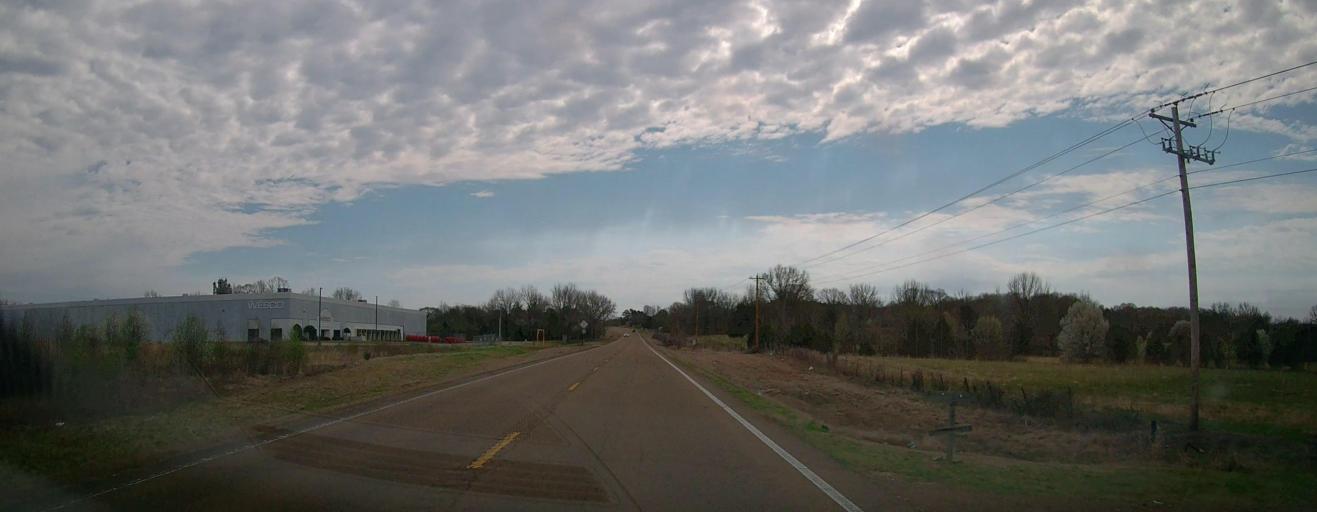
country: US
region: Mississippi
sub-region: Marshall County
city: Byhalia
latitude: 34.8647
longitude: -89.6619
